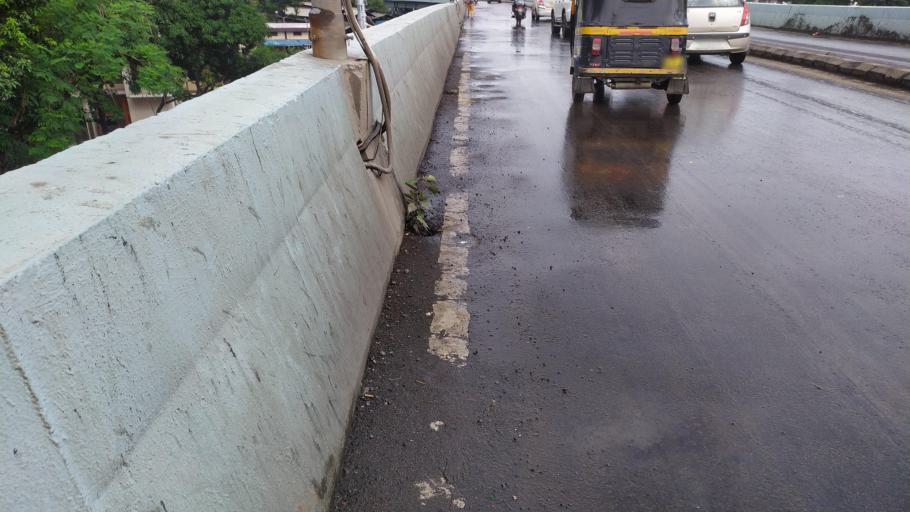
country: IN
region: Maharashtra
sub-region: Mumbai Suburban
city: Borivli
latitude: 19.2381
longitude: 72.8618
